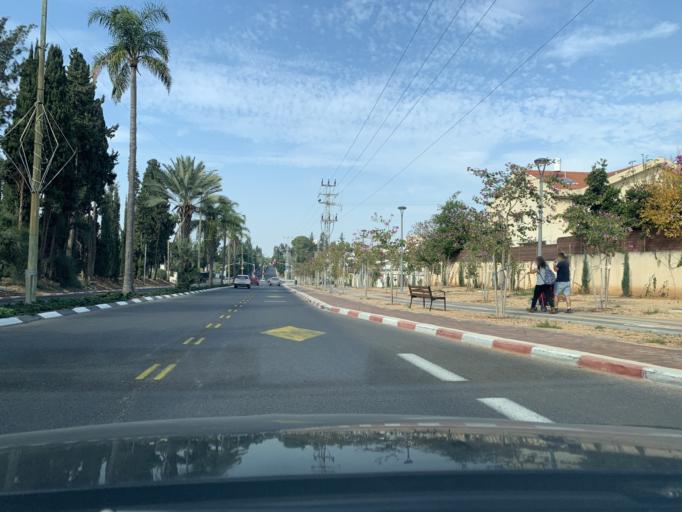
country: IL
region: Tel Aviv
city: Giv`at Shemu'el
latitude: 32.0573
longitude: 34.8505
